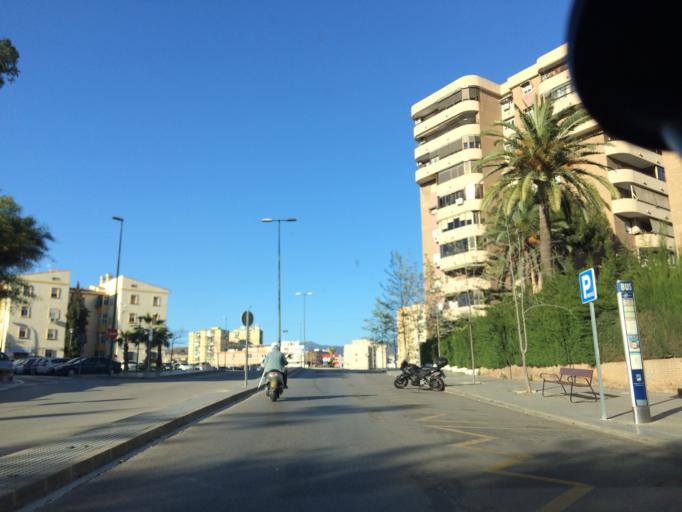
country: ES
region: Andalusia
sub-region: Provincia de Malaga
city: Malaga
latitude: 36.7228
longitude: -4.4483
